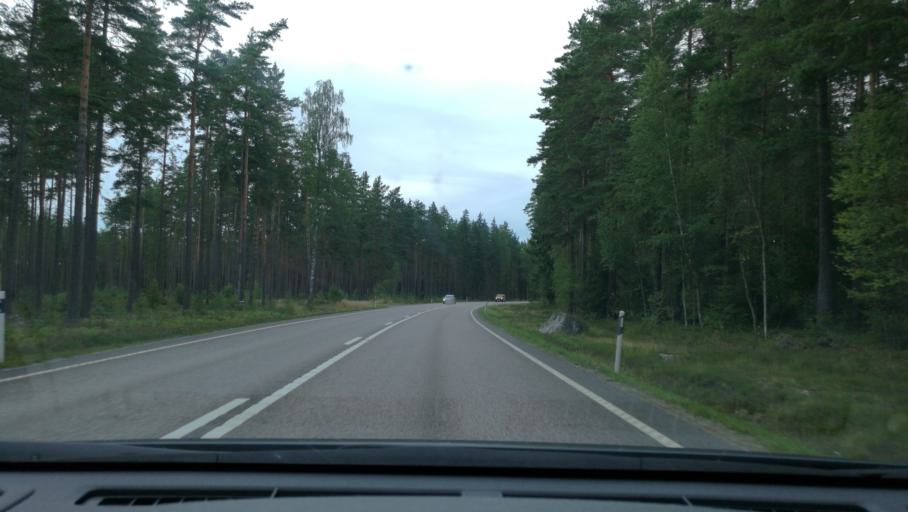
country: SE
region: Vaestmanland
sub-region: Kungsors Kommun
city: Kungsoer
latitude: 59.2147
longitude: 16.0993
